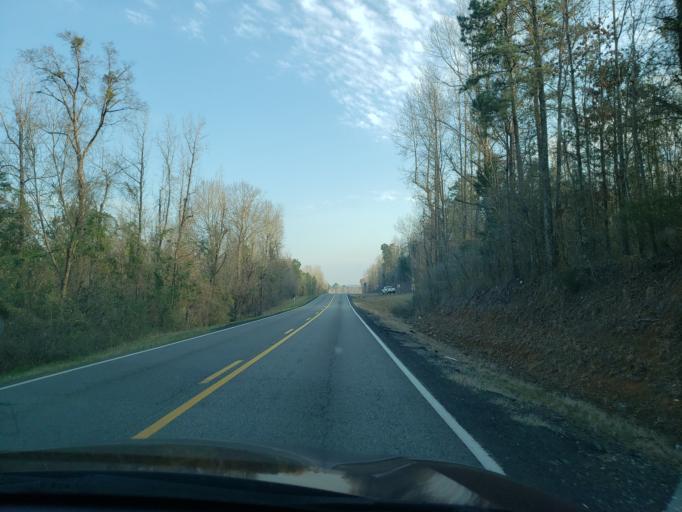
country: US
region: Alabama
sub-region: Hale County
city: Greensboro
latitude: 32.7806
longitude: -87.5877
